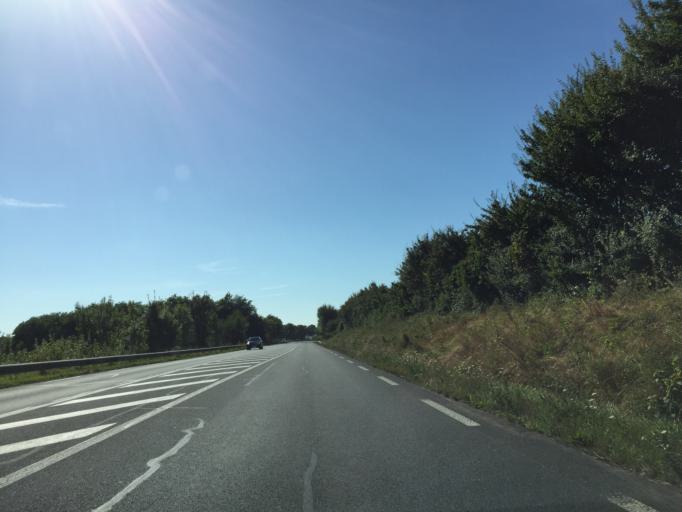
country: FR
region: Lower Normandy
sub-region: Departement du Calvados
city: Lisieux
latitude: 49.1558
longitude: 0.2399
